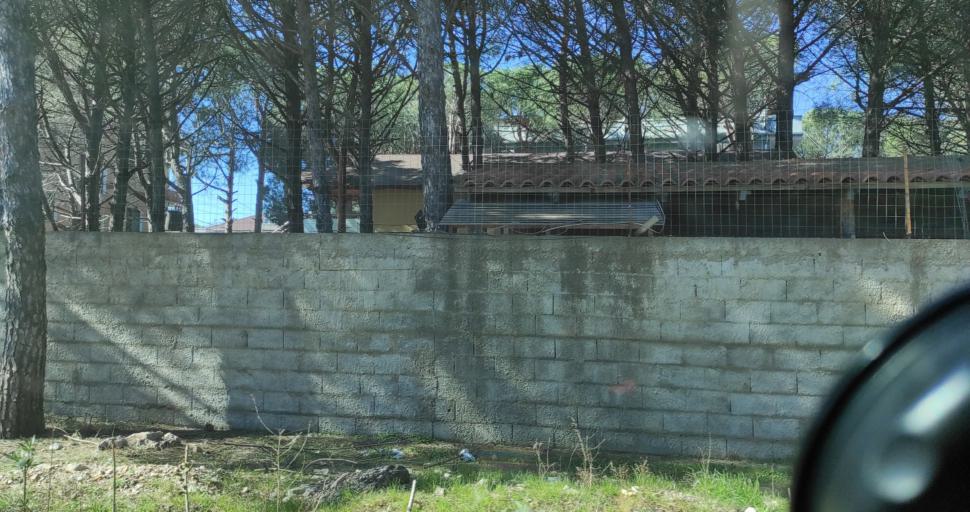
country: AL
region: Shkoder
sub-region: Rrethi i Shkodres
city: Velipoje
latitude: 41.8643
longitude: 19.4154
